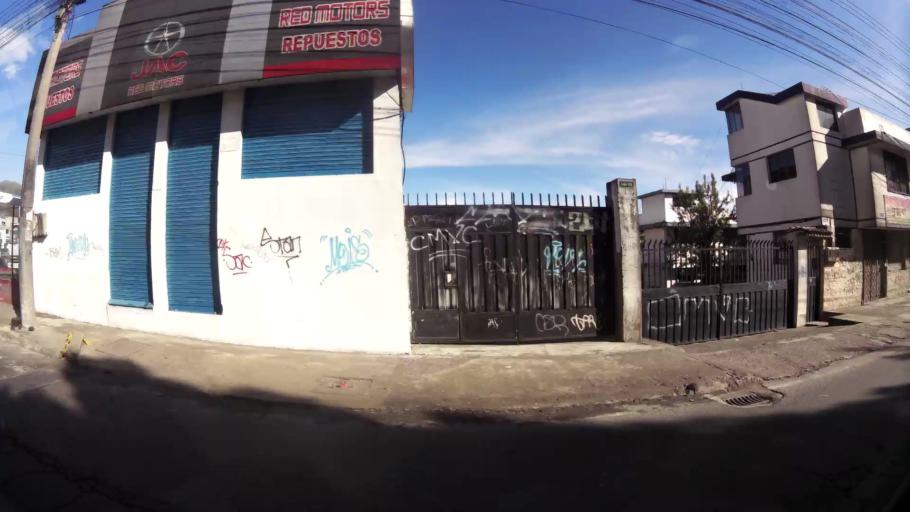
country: EC
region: Pichincha
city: Quito
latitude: -0.3113
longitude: -78.5470
